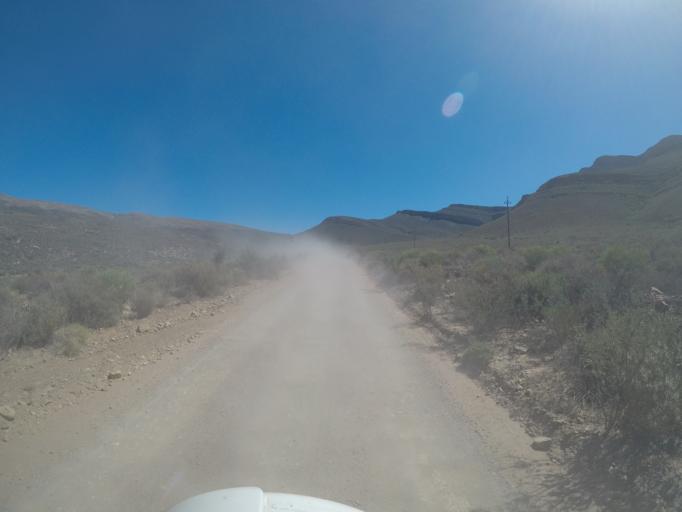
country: ZA
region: Western Cape
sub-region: West Coast District Municipality
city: Clanwilliam
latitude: -32.6287
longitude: 19.3928
